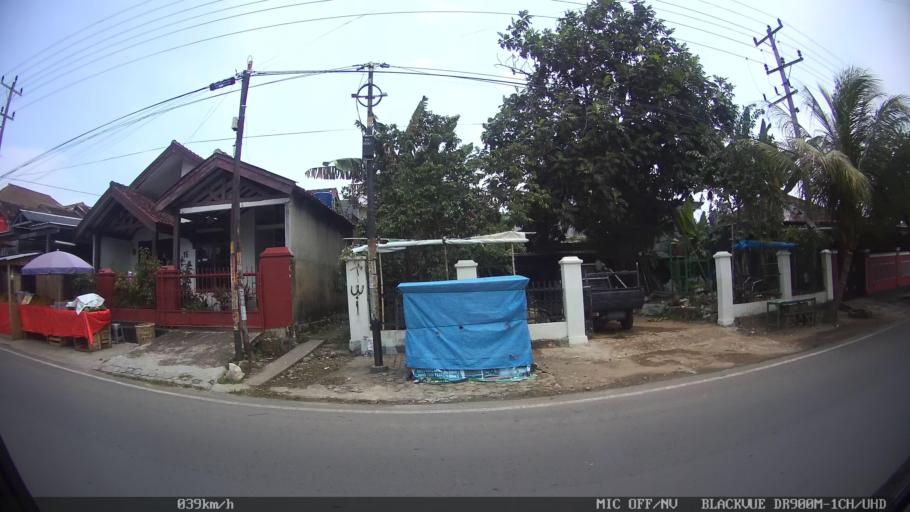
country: ID
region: Lampung
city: Bandarlampung
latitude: -5.4220
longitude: 105.2721
